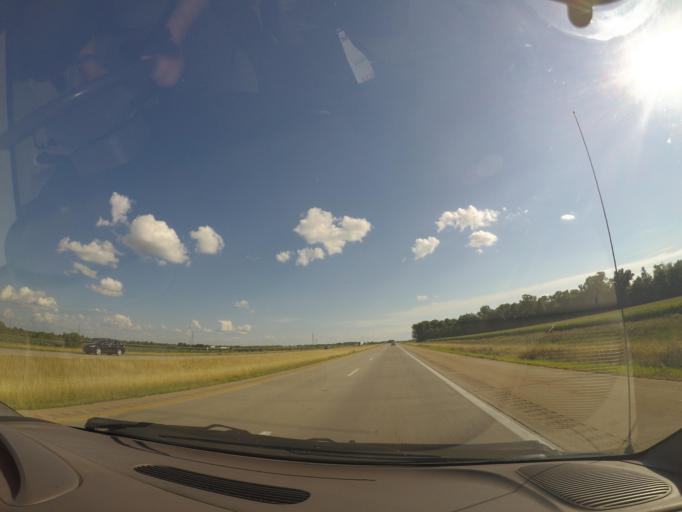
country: US
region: Ohio
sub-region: Lucas County
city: Whitehouse
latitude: 41.4845
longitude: -83.7736
